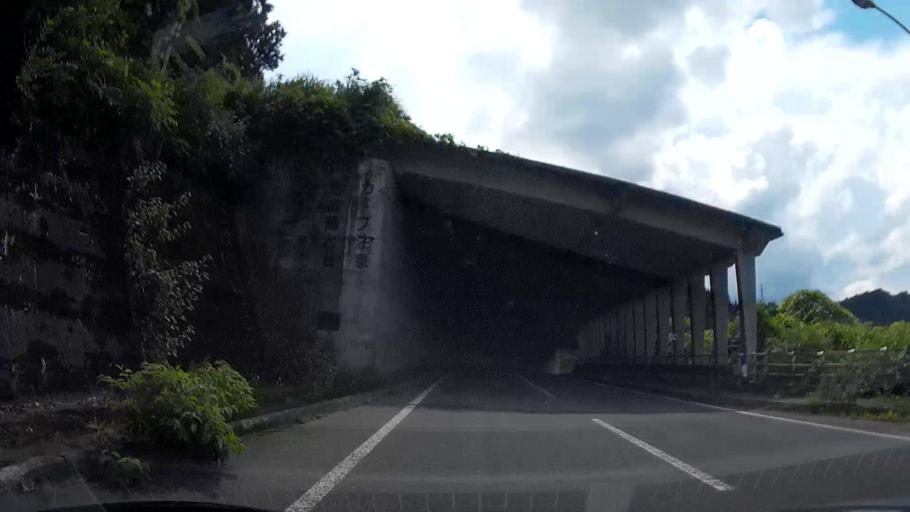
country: JP
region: Niigata
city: Tokamachi
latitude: 36.9935
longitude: 138.6107
